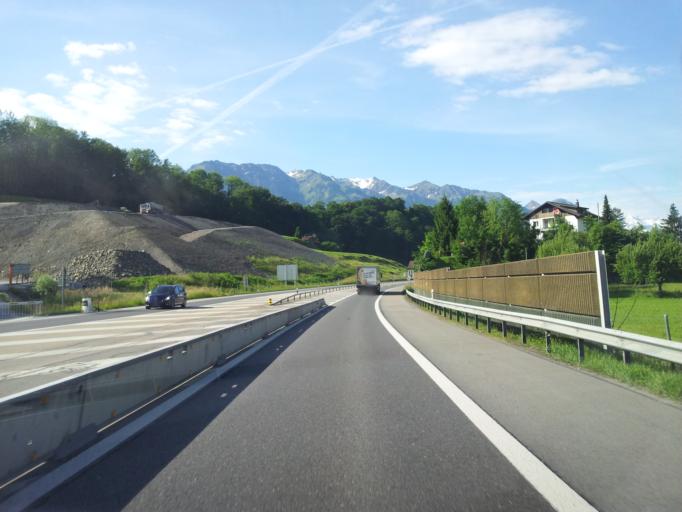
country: CH
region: Obwalden
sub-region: Obwalden
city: Kerns
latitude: 46.9063
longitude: 8.2624
